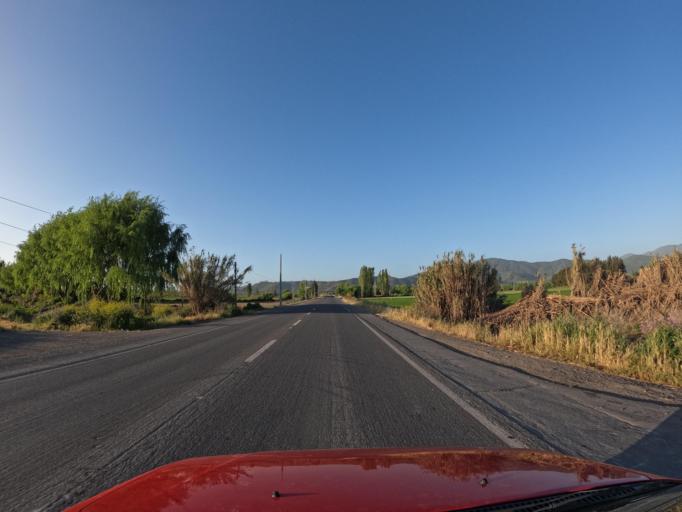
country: CL
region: O'Higgins
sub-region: Provincia de Cachapoal
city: San Vicente
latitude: -34.2902
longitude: -71.3681
